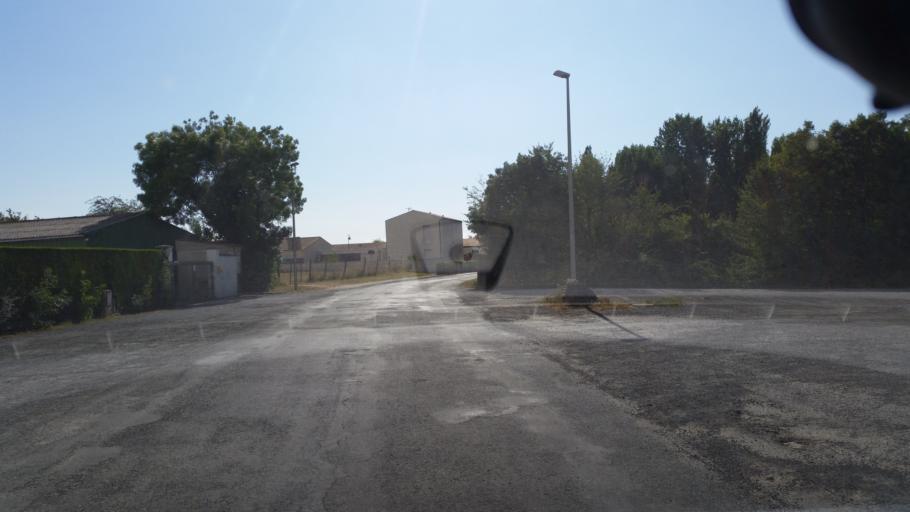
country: FR
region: Poitou-Charentes
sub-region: Departement de la Charente-Maritime
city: Marans
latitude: 46.3096
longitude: -1.0062
